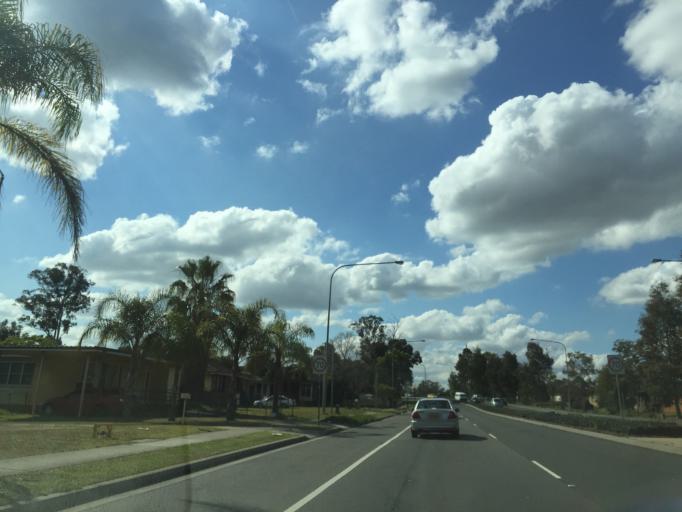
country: AU
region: New South Wales
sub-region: Blacktown
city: Quakers Hill
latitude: -33.7303
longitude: 150.8787
